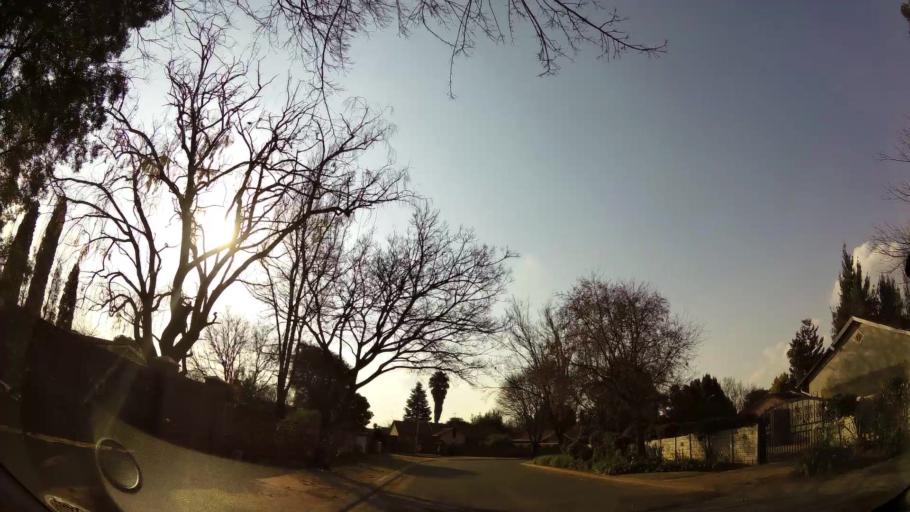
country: ZA
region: Gauteng
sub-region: Ekurhuleni Metropolitan Municipality
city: Benoni
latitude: -26.1265
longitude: 28.3708
